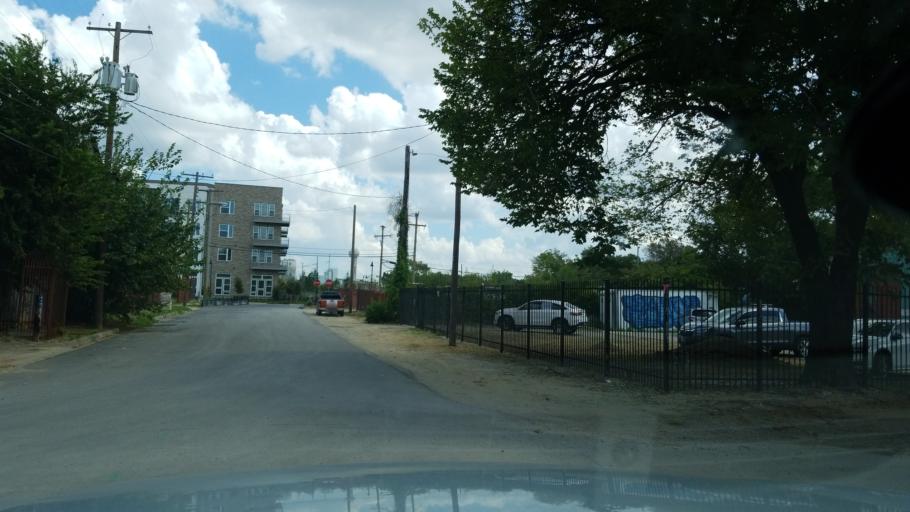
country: US
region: Texas
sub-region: Dallas County
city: Dallas
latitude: 32.7776
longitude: -96.8332
